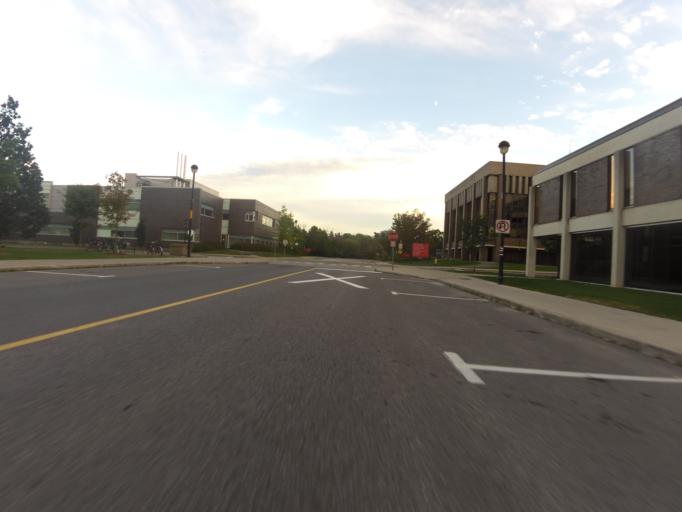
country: CA
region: Ontario
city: Ottawa
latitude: 45.3843
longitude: -75.6943
